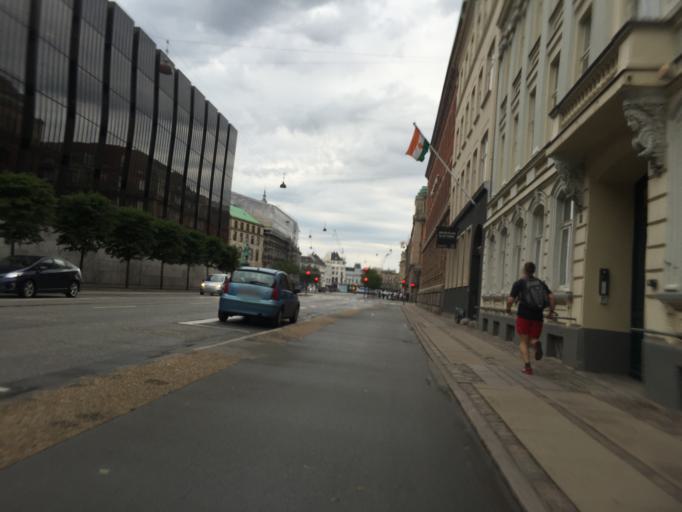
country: DK
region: Capital Region
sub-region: Kobenhavn
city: Christianshavn
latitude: 55.6769
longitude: 12.5867
